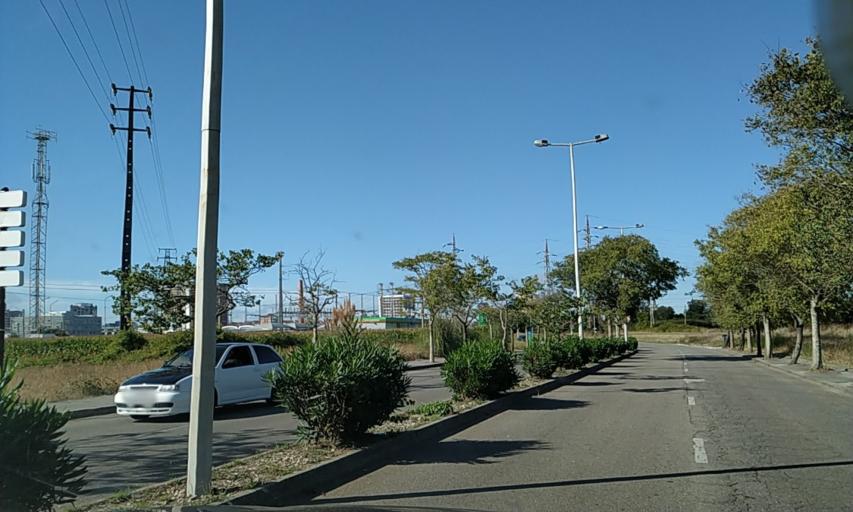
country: PT
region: Aveiro
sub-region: Aveiro
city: Aveiro
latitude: 40.6346
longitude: -8.6429
